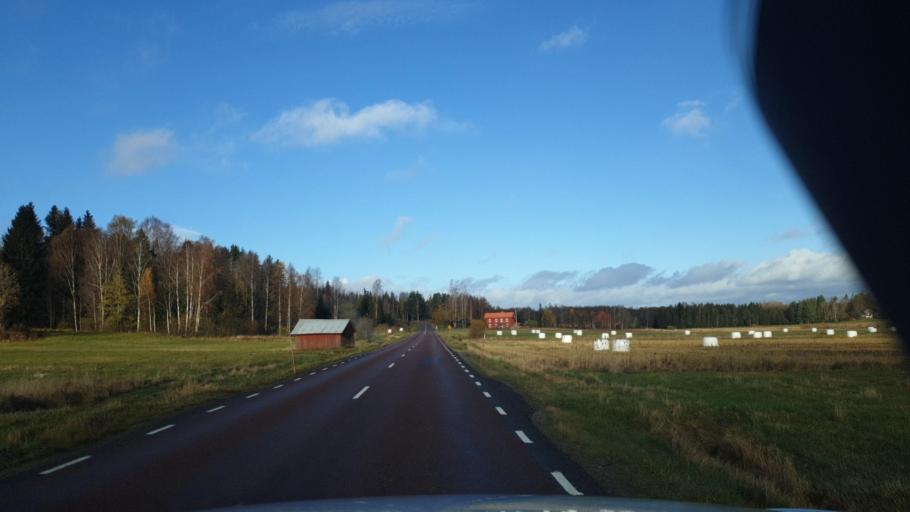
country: SE
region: Vaermland
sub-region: Grums Kommun
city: Grums
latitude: 59.4540
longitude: 12.9689
